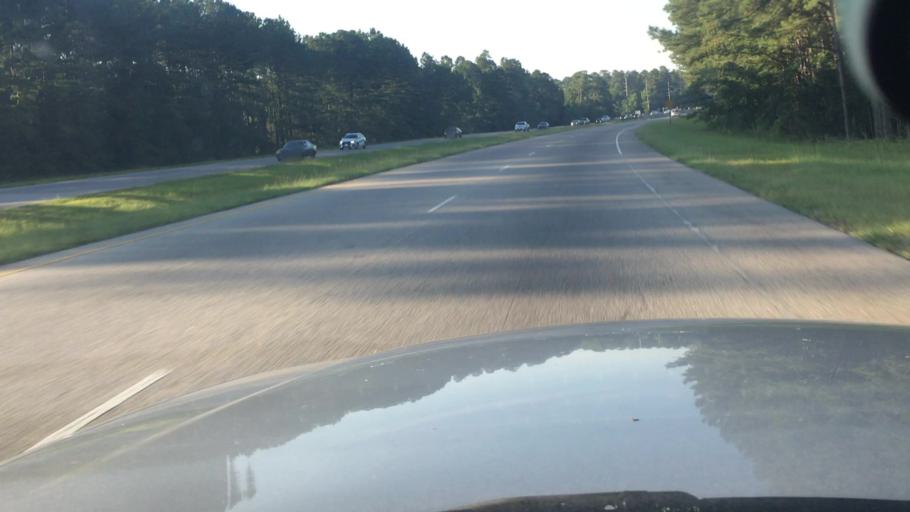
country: US
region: North Carolina
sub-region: Cumberland County
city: Vander
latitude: 34.9597
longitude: -78.8451
